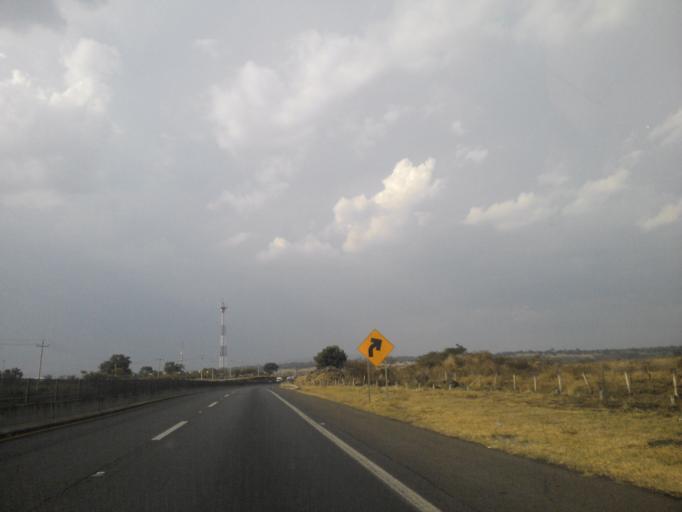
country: MX
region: Jalisco
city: Tepatitlan de Morelos
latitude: 20.8383
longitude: -102.7882
